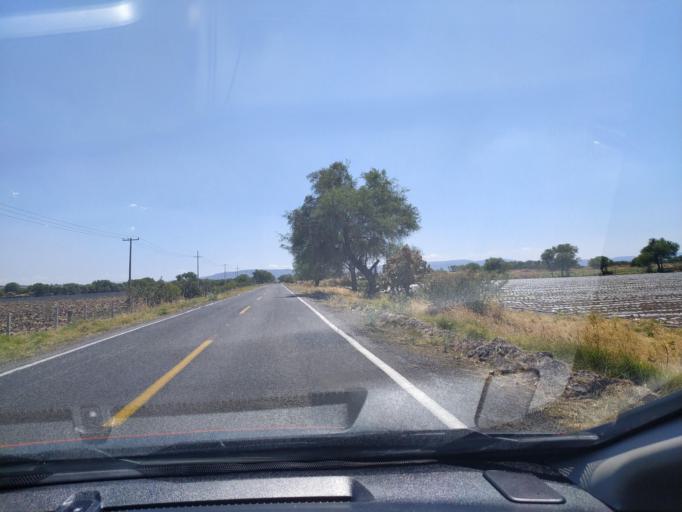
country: MX
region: Guanajuato
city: Ciudad Manuel Doblado
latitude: 20.7693
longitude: -101.8303
